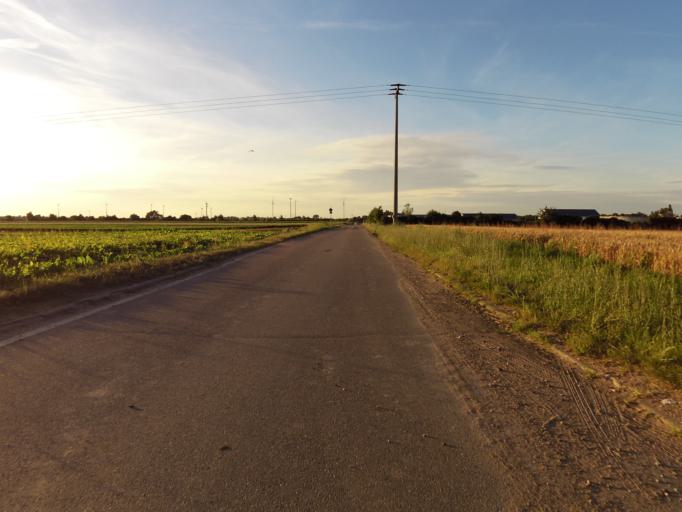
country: DE
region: Rheinland-Pfalz
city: Hessheim
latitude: 49.5541
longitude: 8.3056
